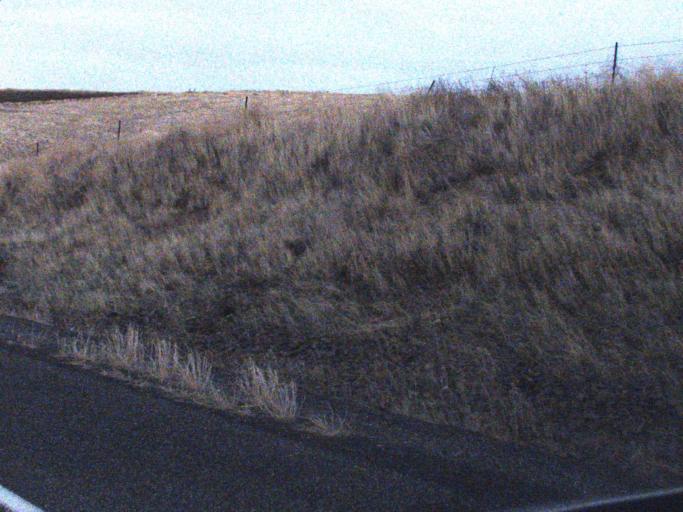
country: US
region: Washington
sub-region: Garfield County
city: Pomeroy
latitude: 46.5425
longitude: -117.7752
